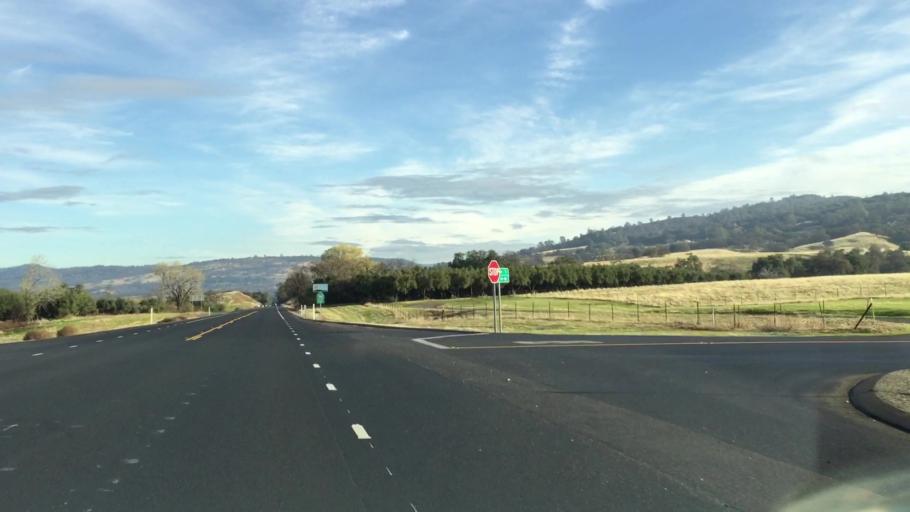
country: US
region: California
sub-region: Butte County
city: Thermalito
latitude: 39.6249
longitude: -121.5937
